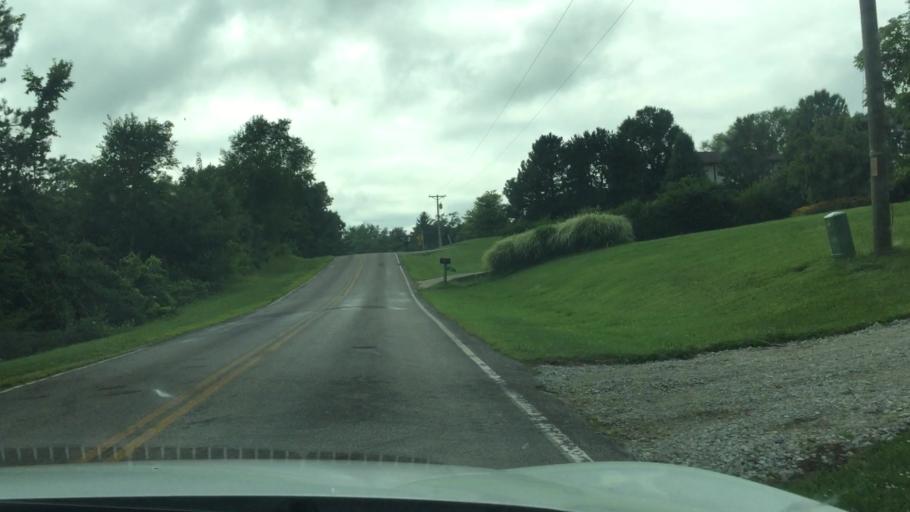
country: US
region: Ohio
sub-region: Champaign County
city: Mechanicsburg
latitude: 40.0603
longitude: -83.6342
